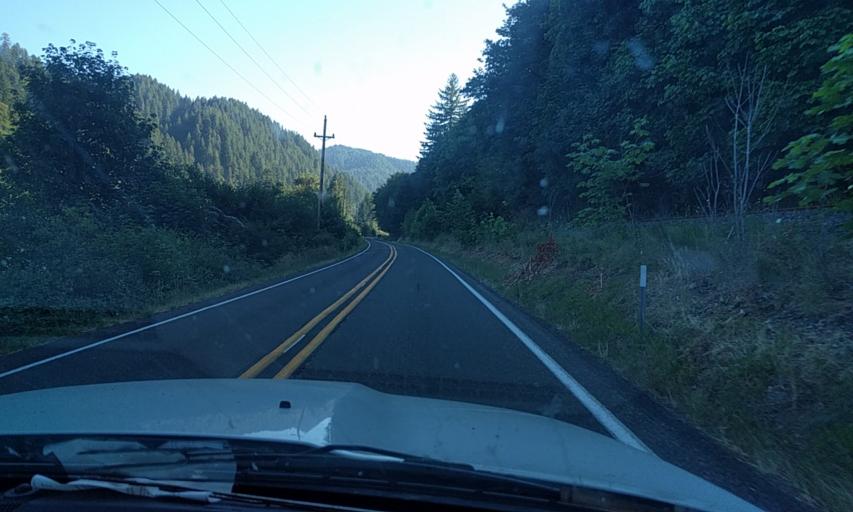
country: US
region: Oregon
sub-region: Lane County
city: Florence
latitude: 44.0732
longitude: -123.8764
